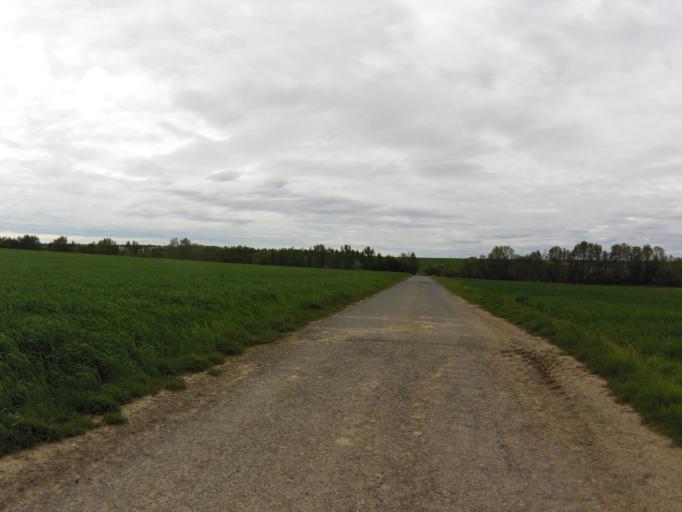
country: DE
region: Bavaria
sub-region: Regierungsbezirk Unterfranken
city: Kurnach
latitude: 49.8444
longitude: 10.0617
